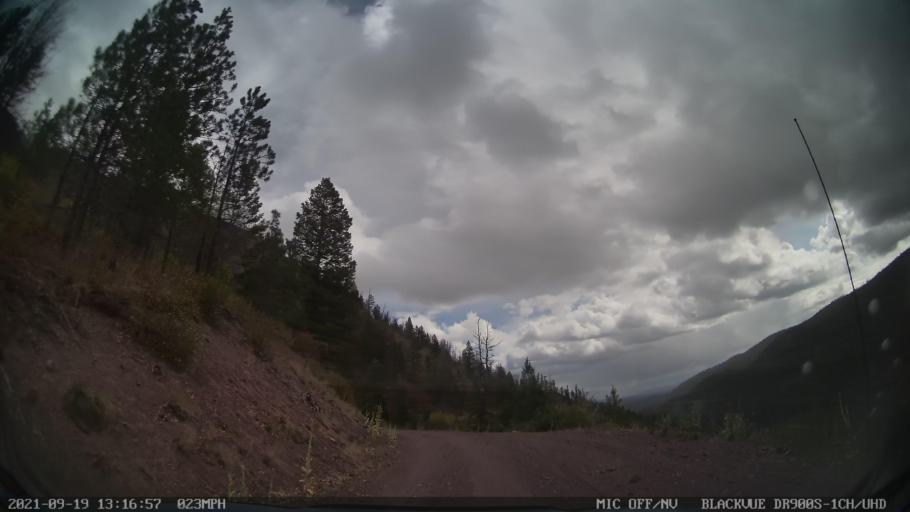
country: US
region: Montana
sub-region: Missoula County
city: Seeley Lake
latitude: 47.1762
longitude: -113.3666
